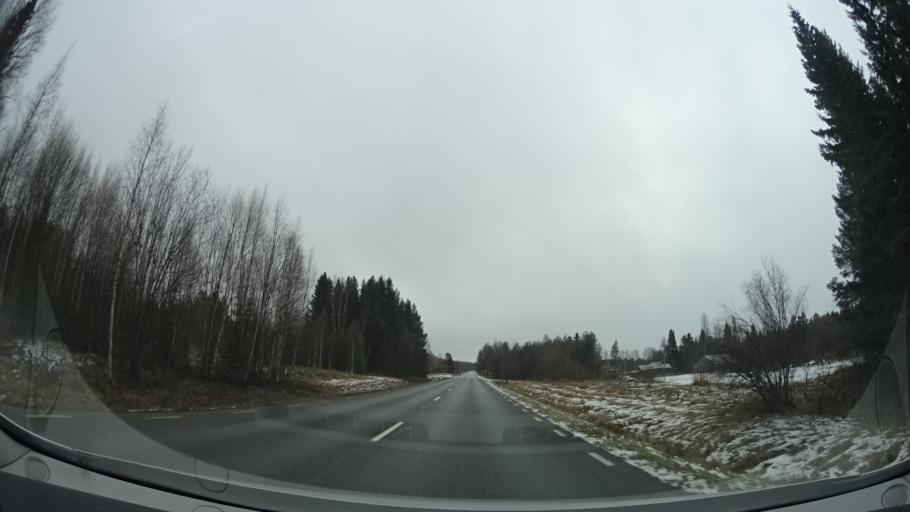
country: SE
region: Jaemtland
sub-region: Stroemsunds Kommun
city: Stroemsund
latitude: 63.8667
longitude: 15.5470
